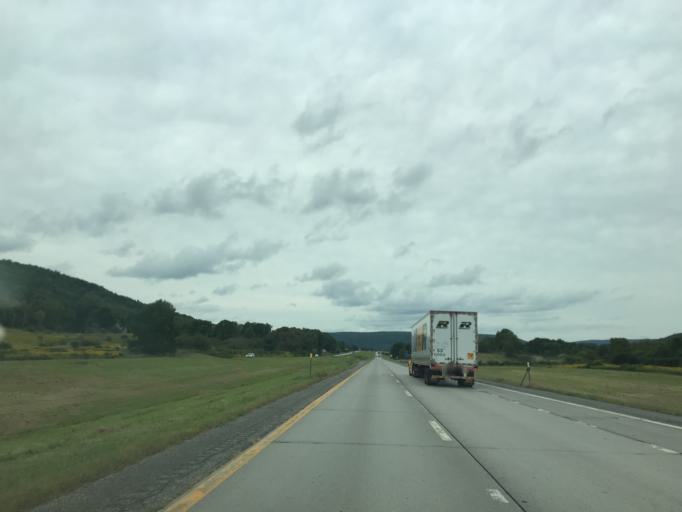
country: US
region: New York
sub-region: Otsego County
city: Oneonta
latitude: 42.4644
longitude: -75.0060
